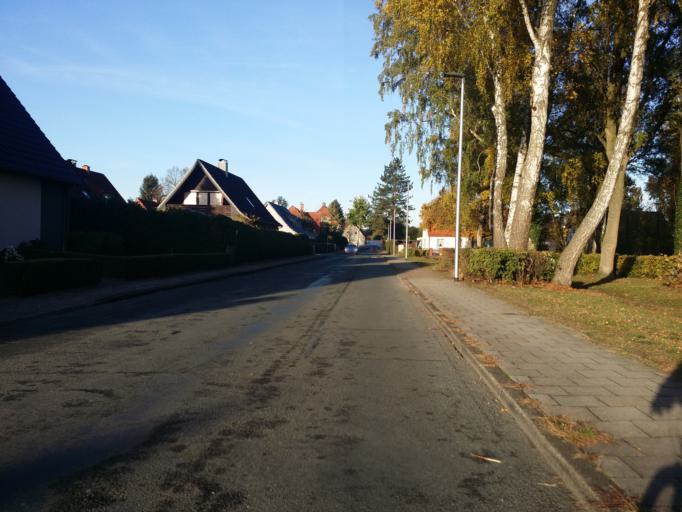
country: DE
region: Lower Saxony
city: Delmenhorst
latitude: 53.0286
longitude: 8.6414
